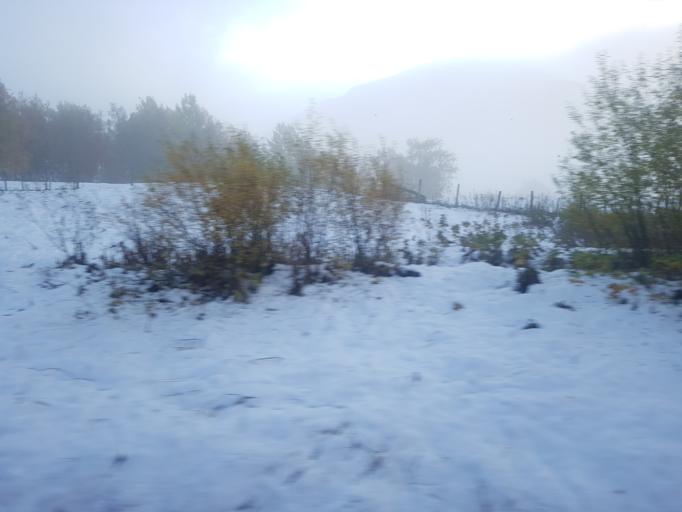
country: NO
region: Sor-Trondelag
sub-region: Oppdal
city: Oppdal
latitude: 62.5727
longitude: 9.6490
